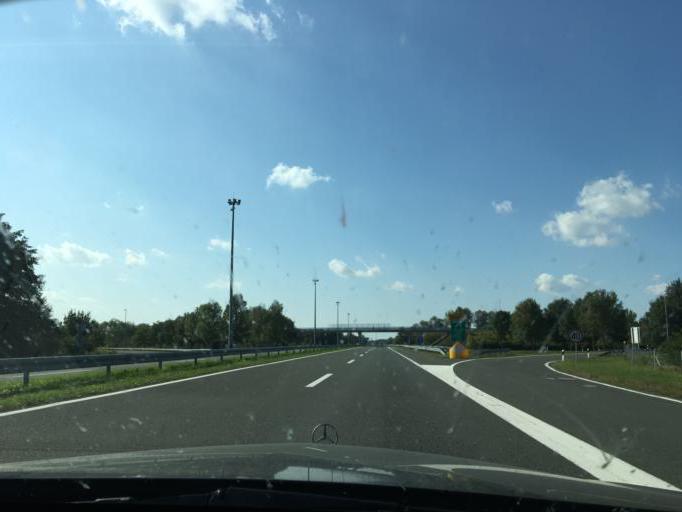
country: HR
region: Medimurska
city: Gorican
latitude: 46.4085
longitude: 16.6692
